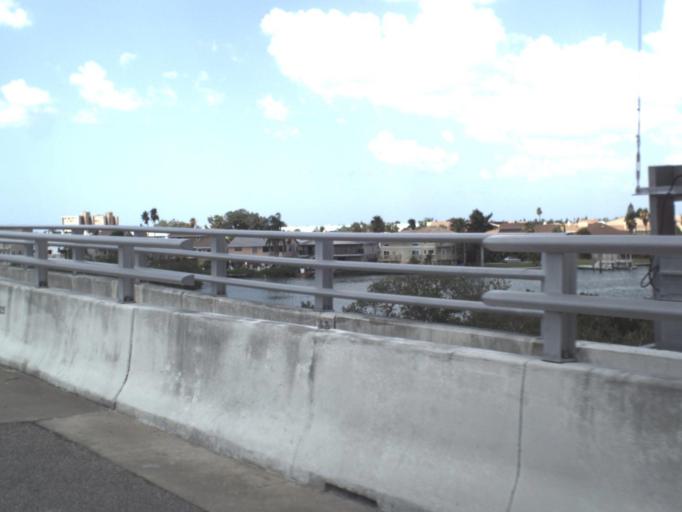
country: US
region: Florida
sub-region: Pinellas County
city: Indian Rocks Beach
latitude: 27.8830
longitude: -82.8447
